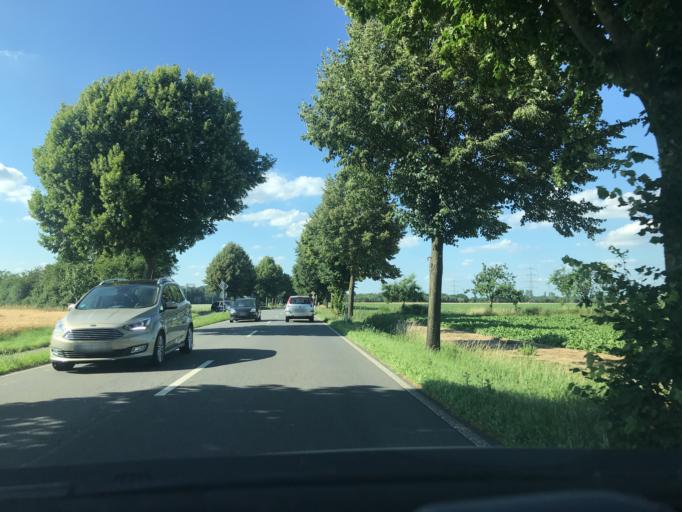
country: DE
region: North Rhine-Westphalia
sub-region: Regierungsbezirk Dusseldorf
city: Neubrueck
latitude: 51.1434
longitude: 6.6792
